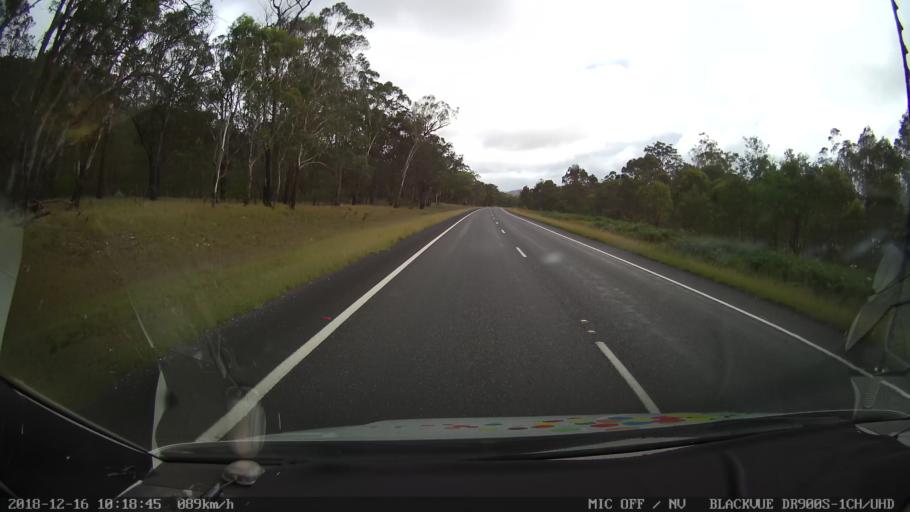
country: AU
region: New South Wales
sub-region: Tenterfield Municipality
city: Carrolls Creek
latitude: -29.2396
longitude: 152.0000
